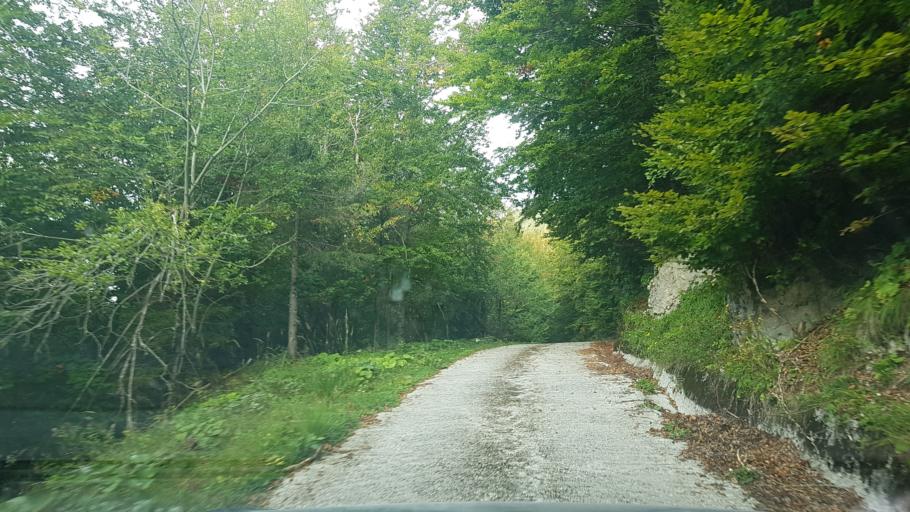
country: SI
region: Bovec
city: Bovec
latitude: 46.4048
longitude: 13.5109
